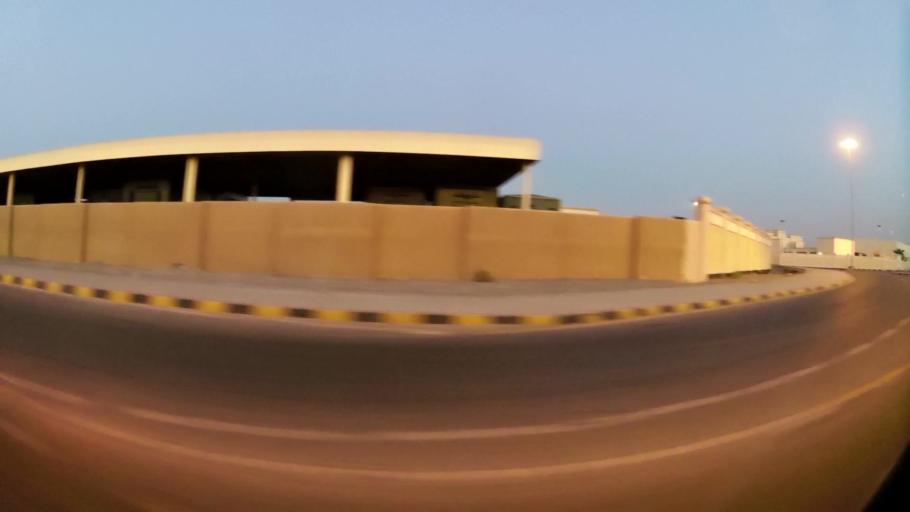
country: OM
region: Muhafazat Masqat
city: As Sib al Jadidah
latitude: 23.6656
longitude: 58.1829
